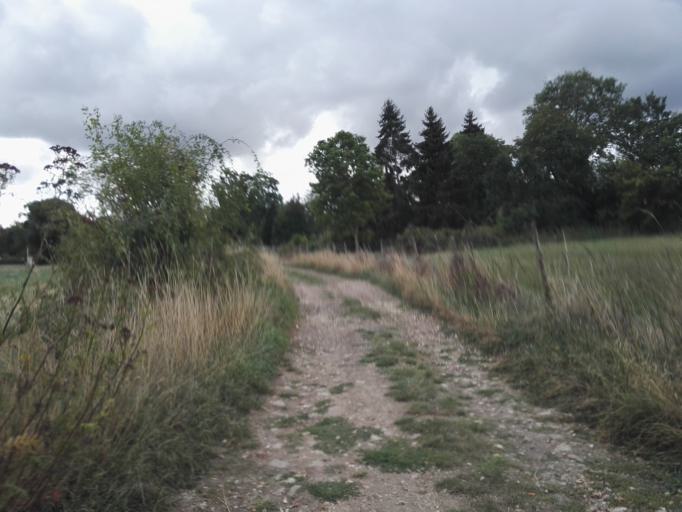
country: FR
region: Haute-Normandie
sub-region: Departement de l'Eure
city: Menilles
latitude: 49.0468
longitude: 1.3408
